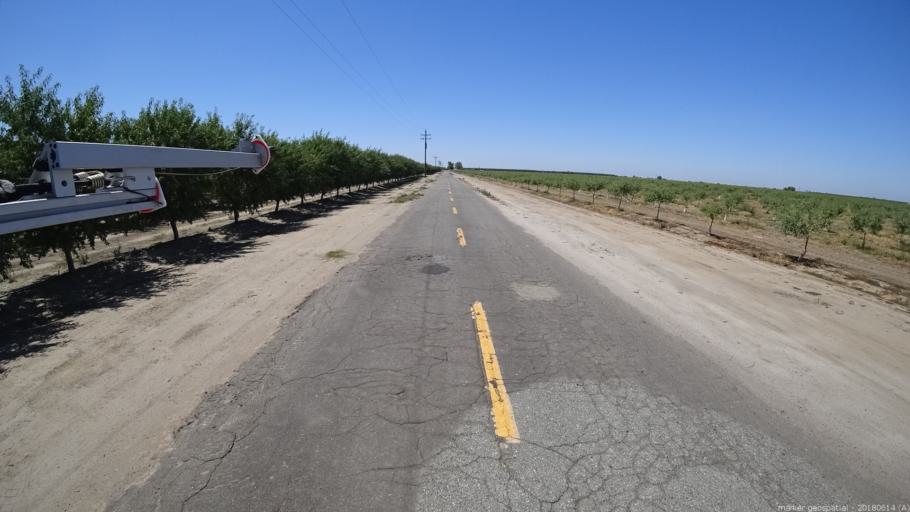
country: US
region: California
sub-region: Madera County
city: Fairmead
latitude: 36.9952
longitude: -120.2477
